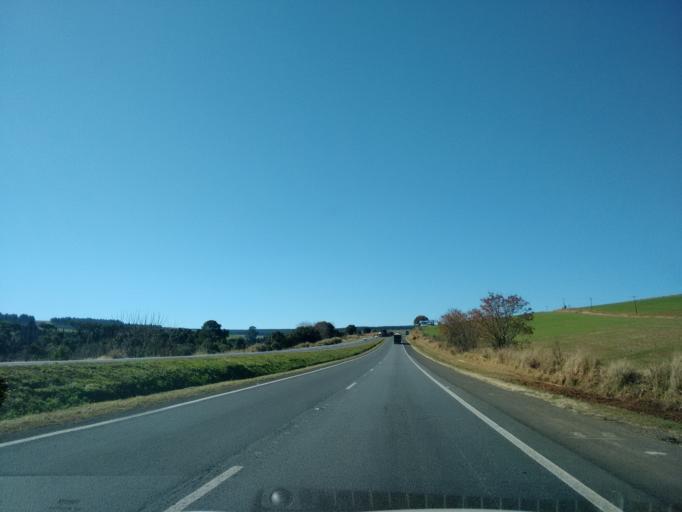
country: BR
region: Parana
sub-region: Palmeira
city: Palmeira
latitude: -25.2664
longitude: -49.9633
